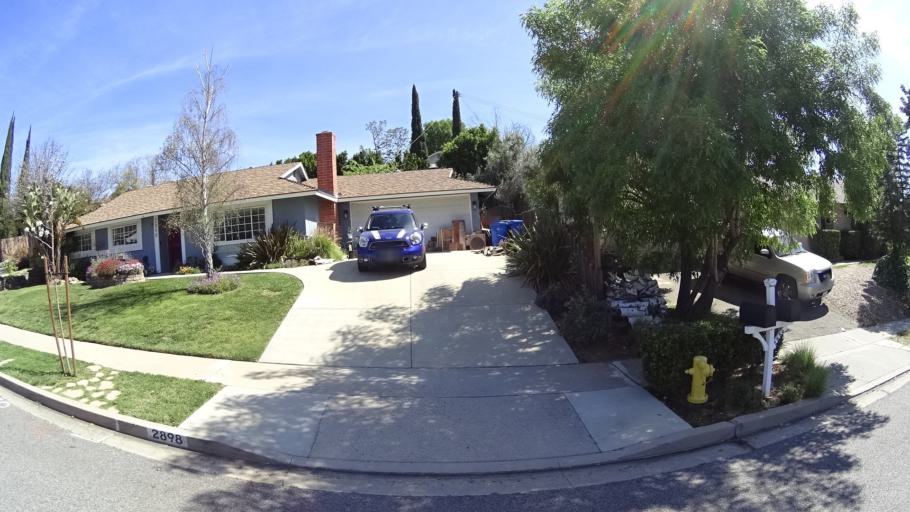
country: US
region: California
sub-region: Ventura County
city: Thousand Oaks
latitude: 34.2189
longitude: -118.8611
